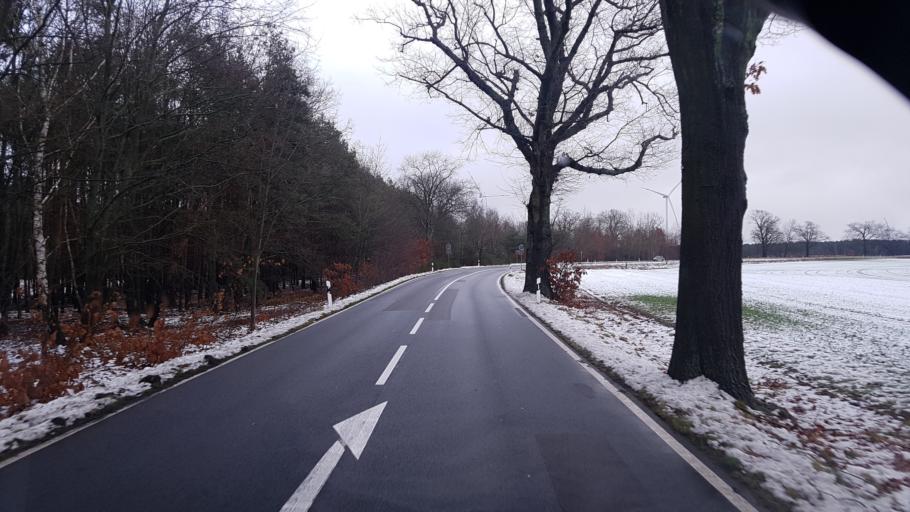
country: DE
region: Brandenburg
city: Schenkendobern
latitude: 51.9691
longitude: 14.5821
